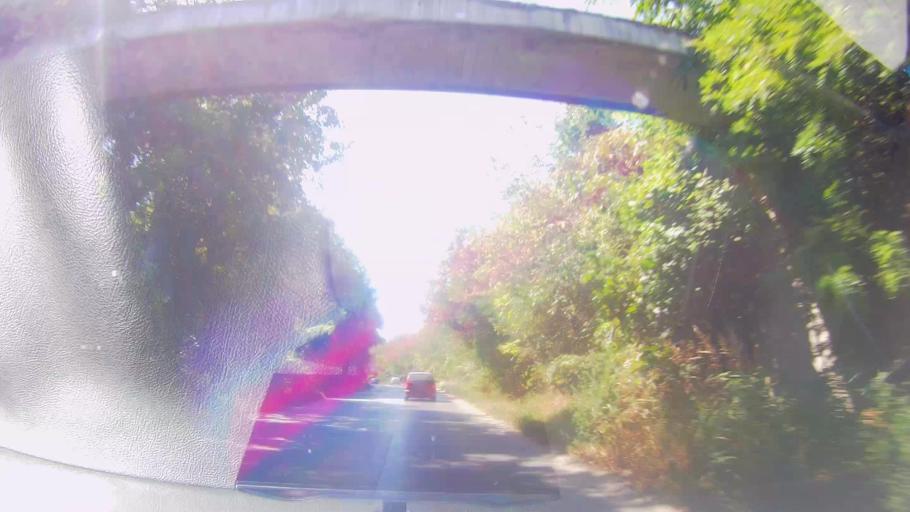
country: BG
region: Veliko Turnovo
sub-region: Obshtina Gorna Oryakhovitsa
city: Purvomaytsi
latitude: 43.1682
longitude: 25.6188
